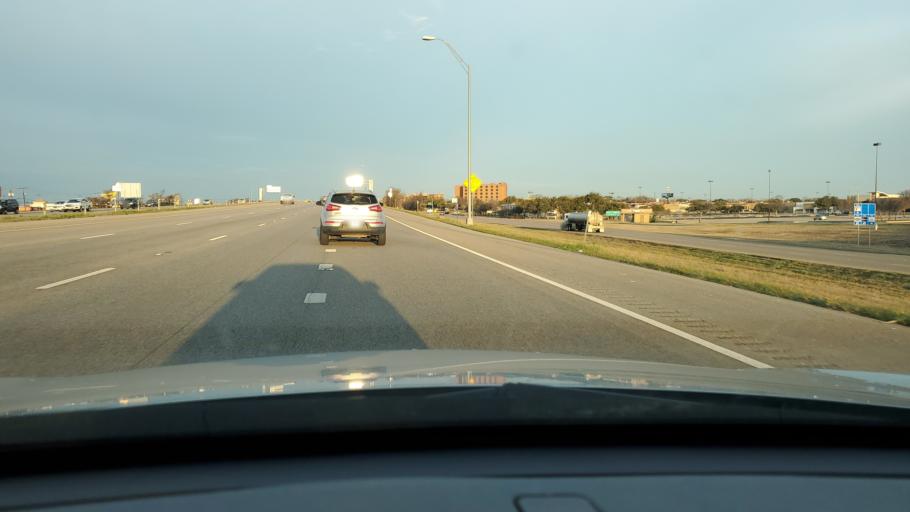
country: US
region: Texas
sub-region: Bell County
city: Killeen
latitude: 31.0896
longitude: -97.7169
